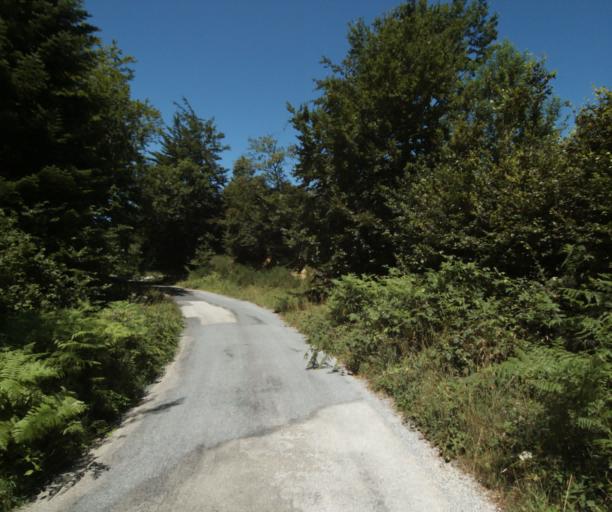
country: FR
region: Languedoc-Roussillon
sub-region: Departement de l'Aude
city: Cuxac-Cabardes
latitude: 43.4091
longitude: 2.1998
